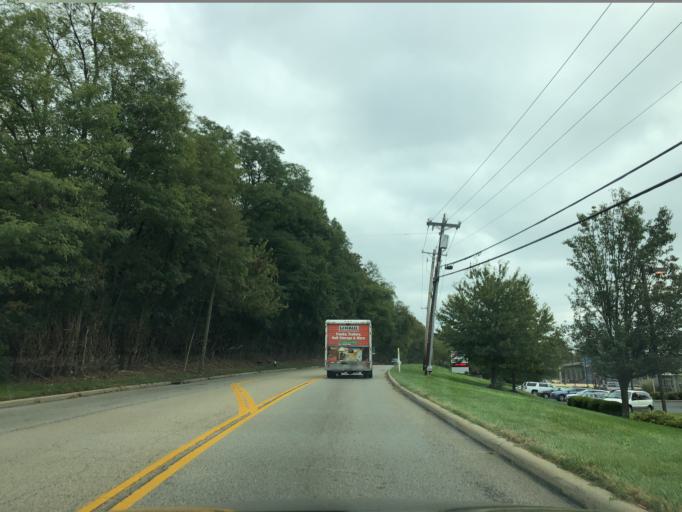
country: US
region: Ohio
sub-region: Hamilton County
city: The Village of Indian Hill
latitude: 39.2547
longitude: -84.2944
